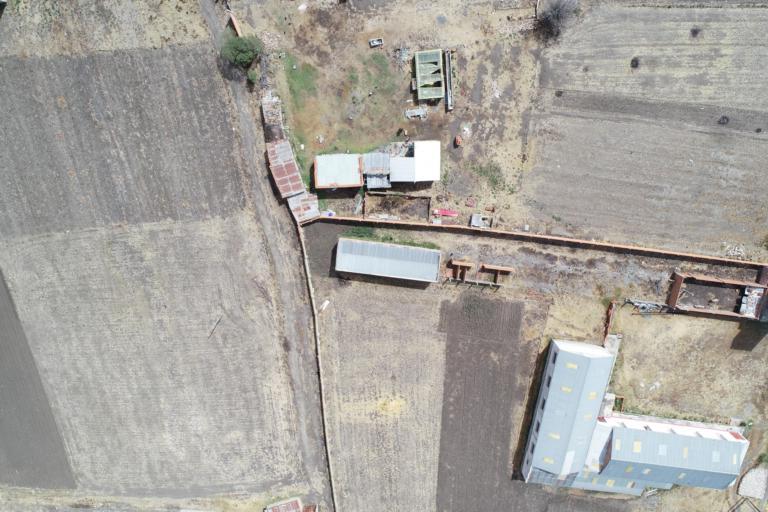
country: BO
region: La Paz
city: Achacachi
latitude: -16.0372
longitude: -68.6881
